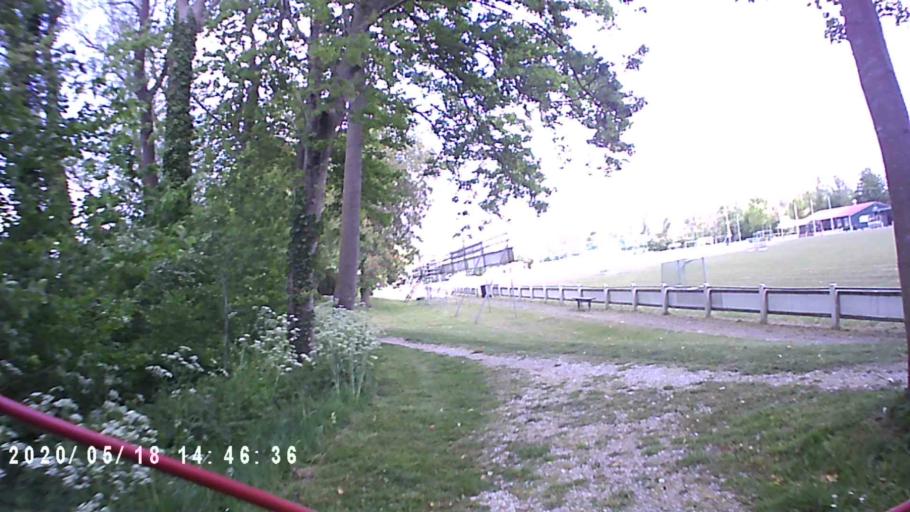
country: NL
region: Groningen
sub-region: Gemeente Winsum
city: Winsum
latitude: 53.3335
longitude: 6.5071
